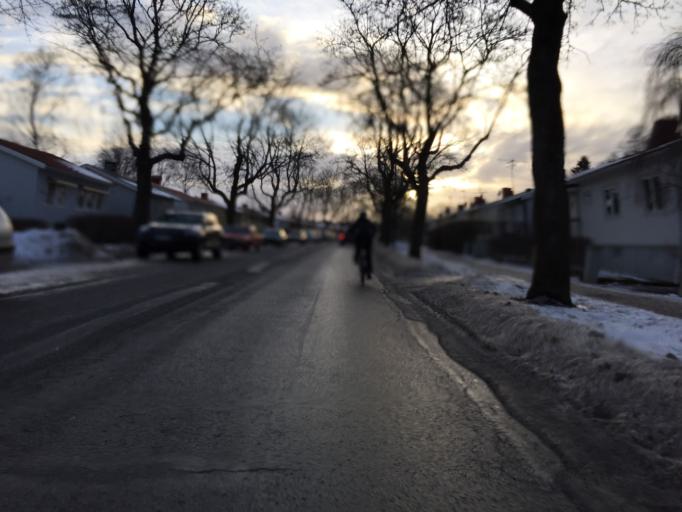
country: SE
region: Stockholm
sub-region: Stockholms Kommun
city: Bromma
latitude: 59.3450
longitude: 17.9190
